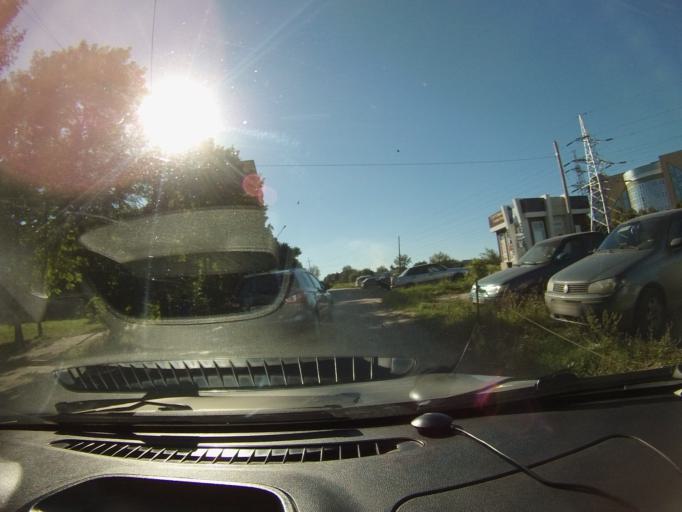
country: RU
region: Tambov
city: Tambov
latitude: 52.7598
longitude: 41.4232
